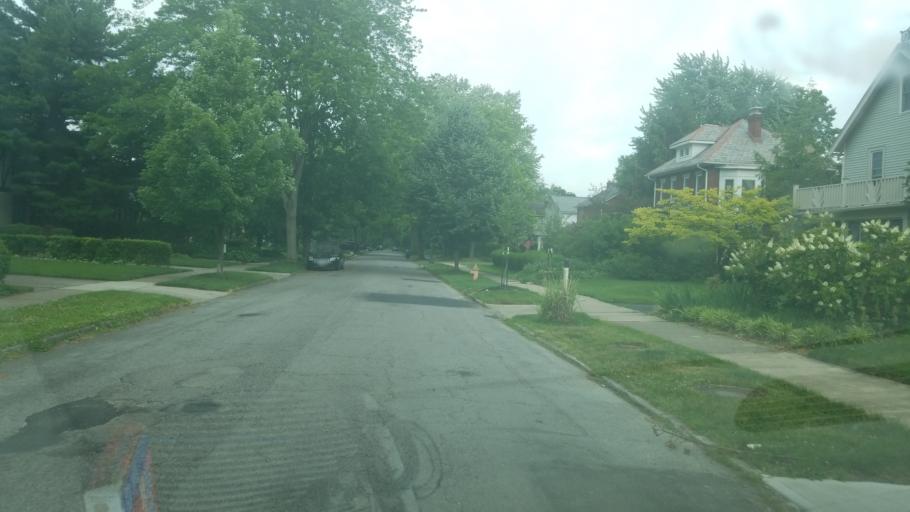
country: US
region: Ohio
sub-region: Franklin County
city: Worthington
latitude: 40.0341
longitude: -83.0057
